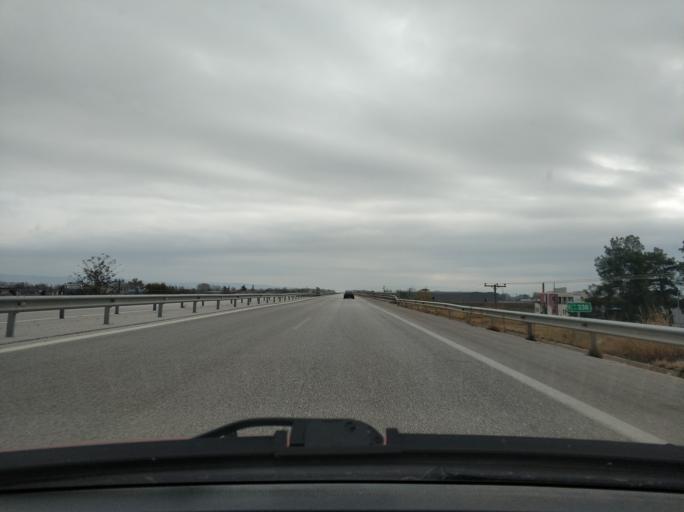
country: GR
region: Central Macedonia
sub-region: Nomos Thessalonikis
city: Kavallari
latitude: 40.7359
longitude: 23.0341
